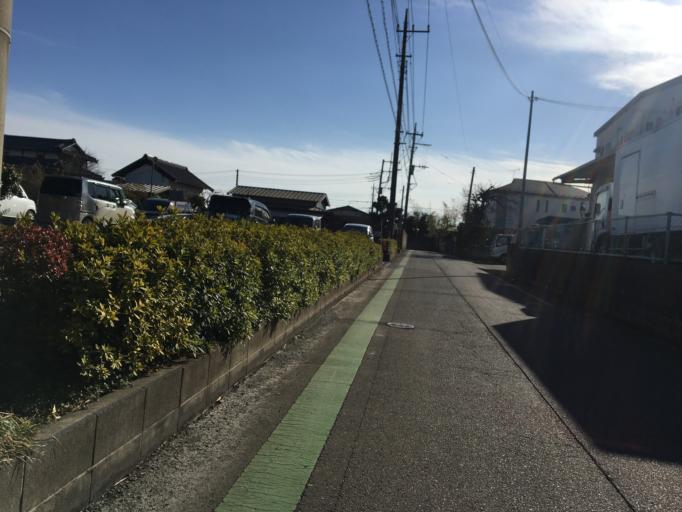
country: JP
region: Saitama
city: Oi
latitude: 35.8288
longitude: 139.5473
